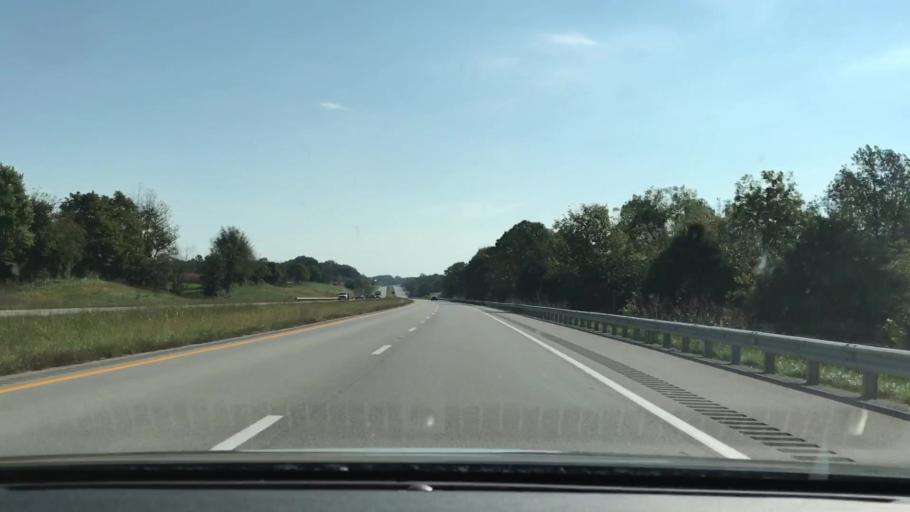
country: US
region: Kentucky
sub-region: Pulaski County
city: Somerset
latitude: 37.0970
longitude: -84.7493
